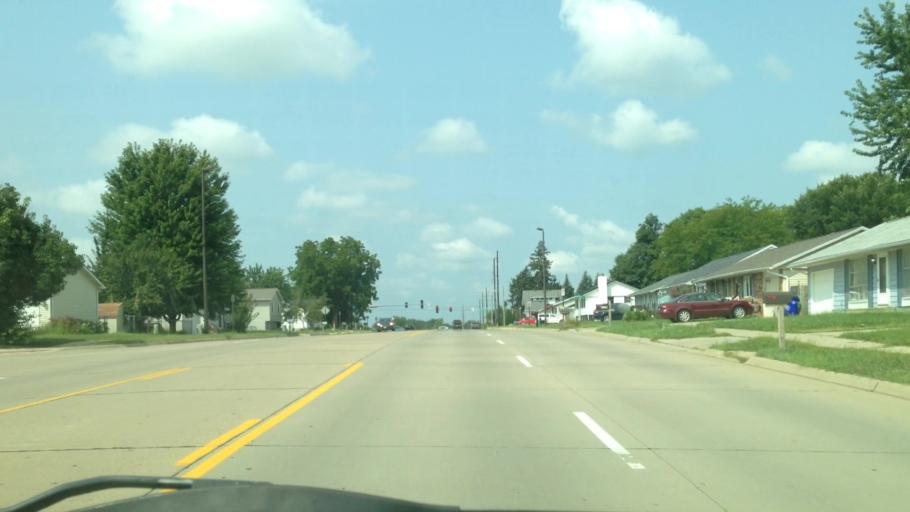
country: US
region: Iowa
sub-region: Linn County
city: Fairfax
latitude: 41.9457
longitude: -91.7130
